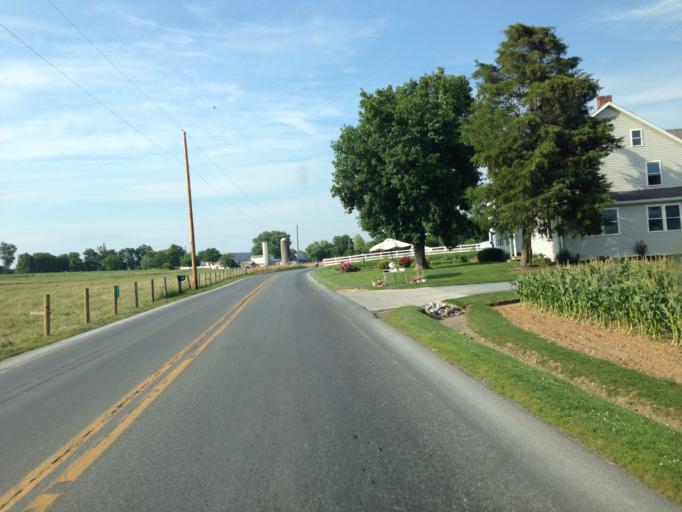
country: US
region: Pennsylvania
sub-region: Lancaster County
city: Brownstown
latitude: 40.0600
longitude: -76.2125
